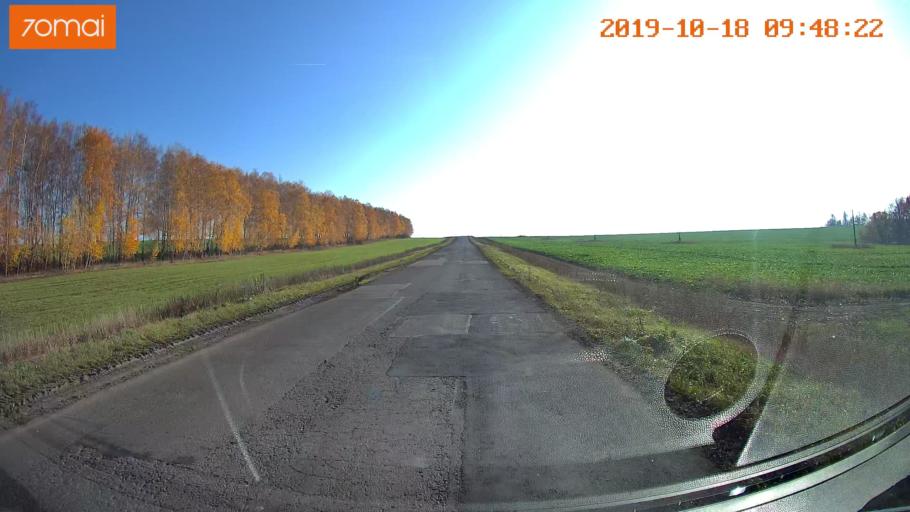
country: RU
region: Tula
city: Kazachka
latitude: 53.3182
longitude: 38.2477
